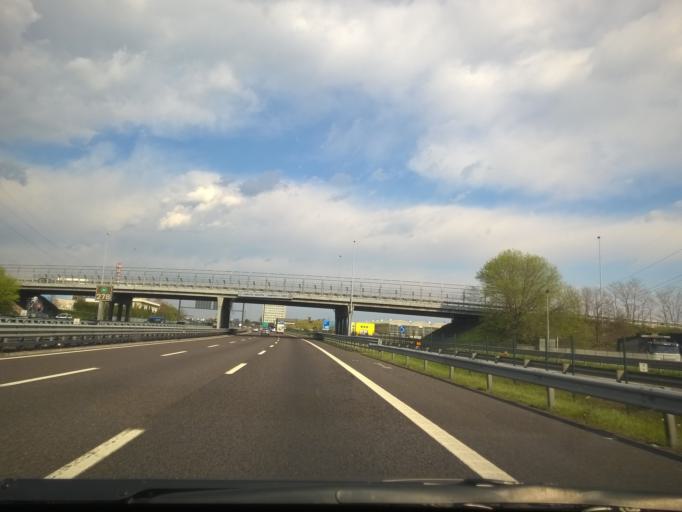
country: IT
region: Veneto
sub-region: Provincia di Verona
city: Beccacivetta-Azzano
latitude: 45.3969
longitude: 10.9791
